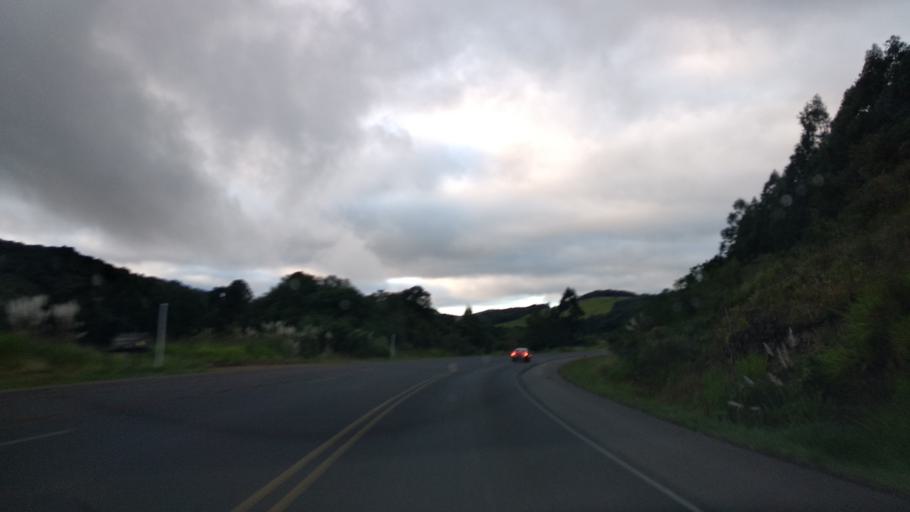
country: BR
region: Santa Catarina
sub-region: Campos Novos
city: Campos Novos
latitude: -27.4539
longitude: -50.9913
